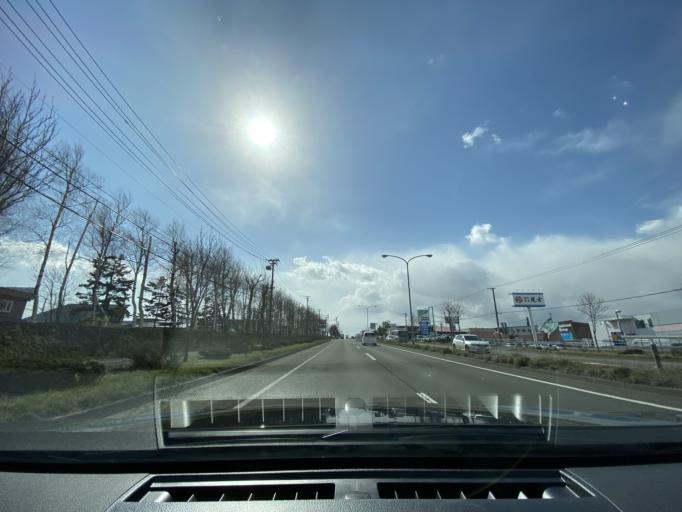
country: JP
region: Hokkaido
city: Kitahiroshima
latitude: 42.9650
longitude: 141.4867
